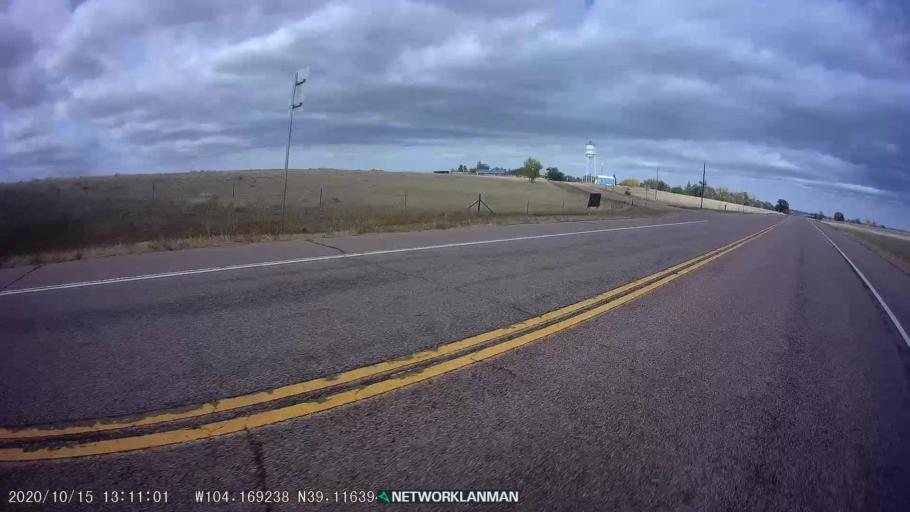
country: US
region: Colorado
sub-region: El Paso County
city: Ellicott
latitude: 39.1168
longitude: -104.1689
